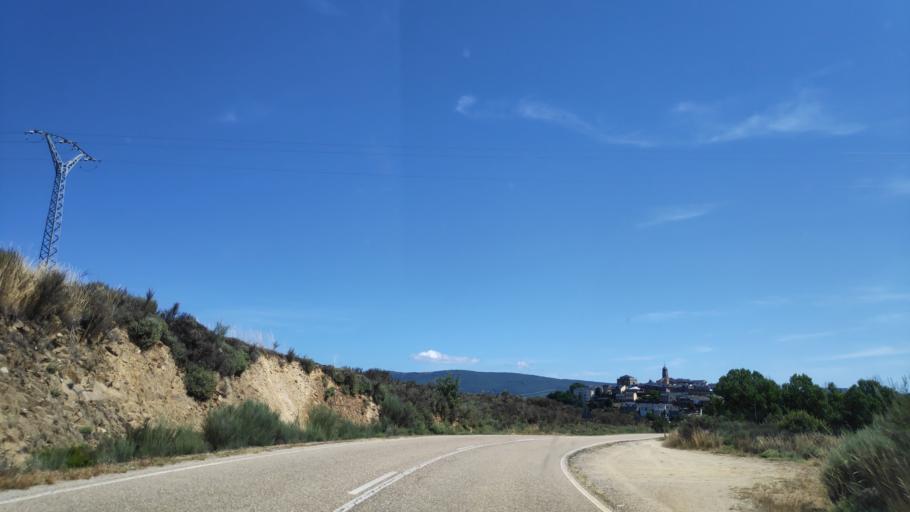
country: ES
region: Castille and Leon
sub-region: Provincia de Zamora
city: Puebla de Sanabria
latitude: 42.0508
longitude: -6.6416
